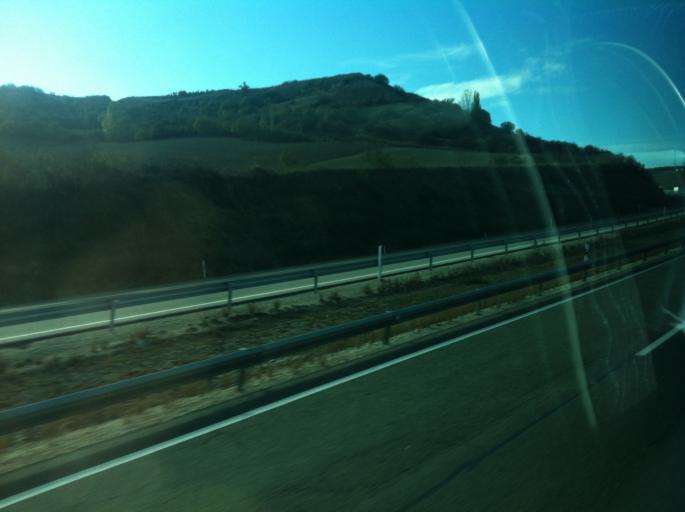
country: ES
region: Castille and Leon
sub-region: Provincia de Burgos
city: Monasterio de Rodilla
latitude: 42.4526
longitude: -3.4712
